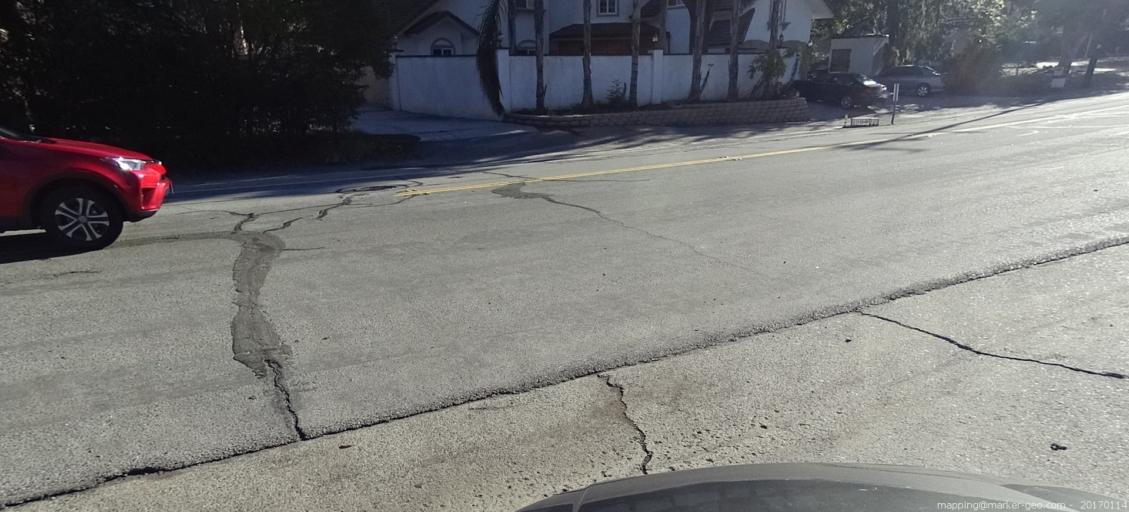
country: US
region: California
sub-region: Orange County
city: North Tustin
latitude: 33.7829
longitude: -117.7958
